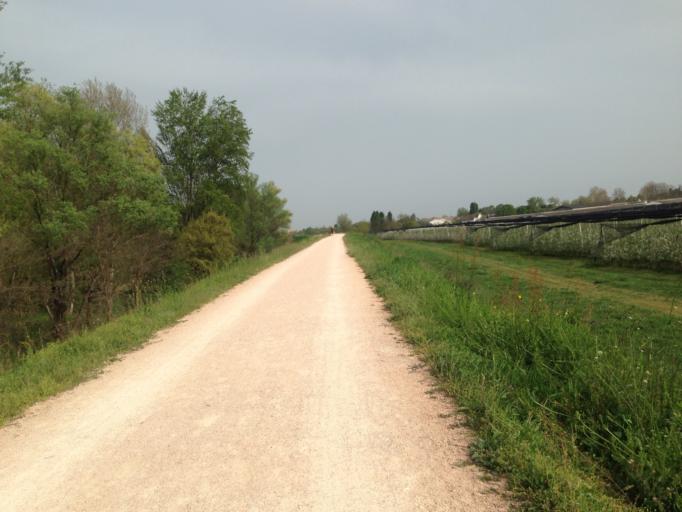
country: IT
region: Veneto
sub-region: Provincia di Verona
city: Zevio
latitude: 45.3780
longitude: 11.1155
